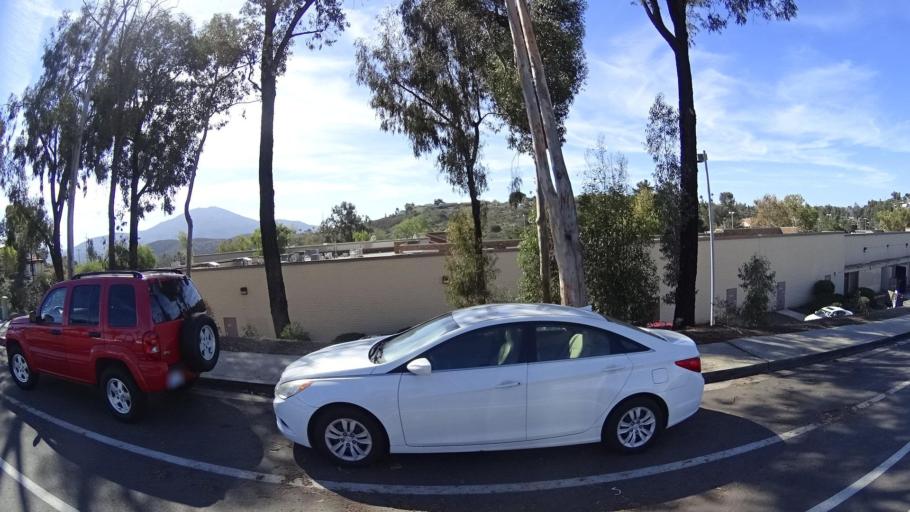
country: US
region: California
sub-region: San Diego County
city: Casa de Oro-Mount Helix
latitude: 32.7477
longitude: -116.9587
